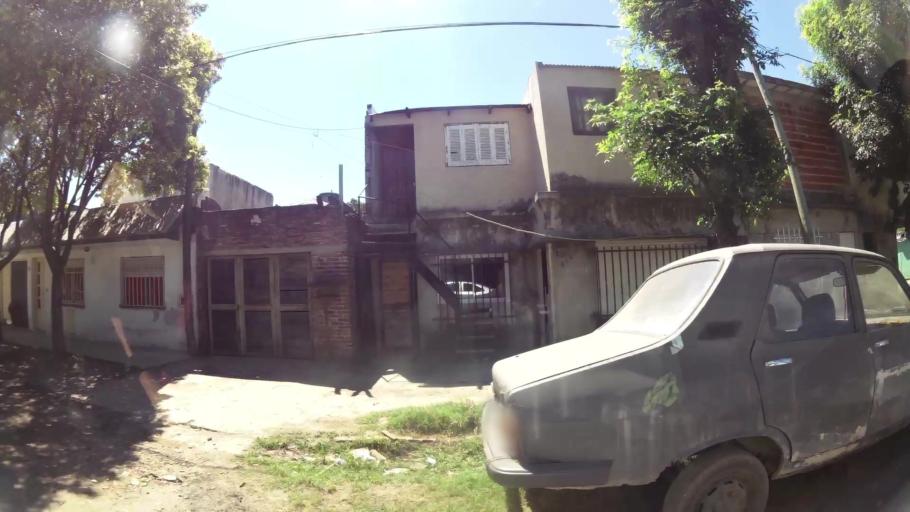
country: AR
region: Santa Fe
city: Perez
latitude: -32.9515
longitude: -60.7178
